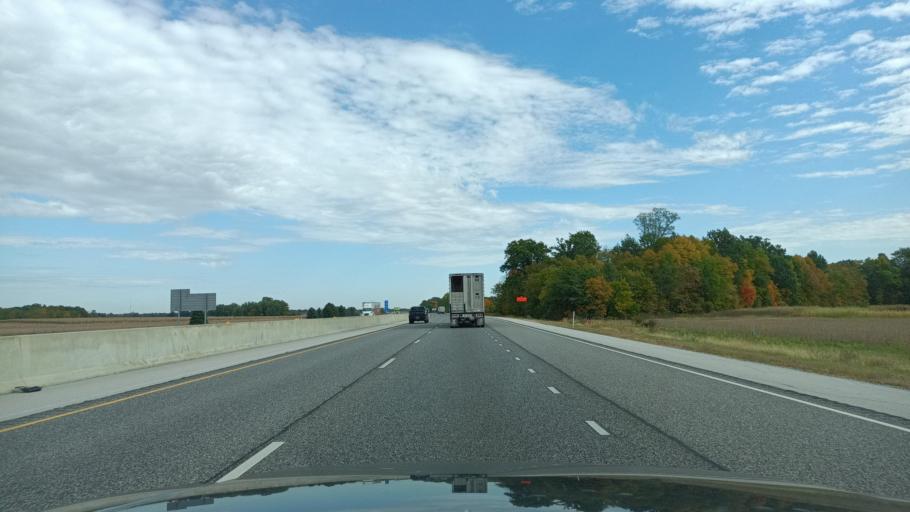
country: US
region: Indiana
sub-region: Wells County
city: Ossian
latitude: 40.9702
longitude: -85.1188
